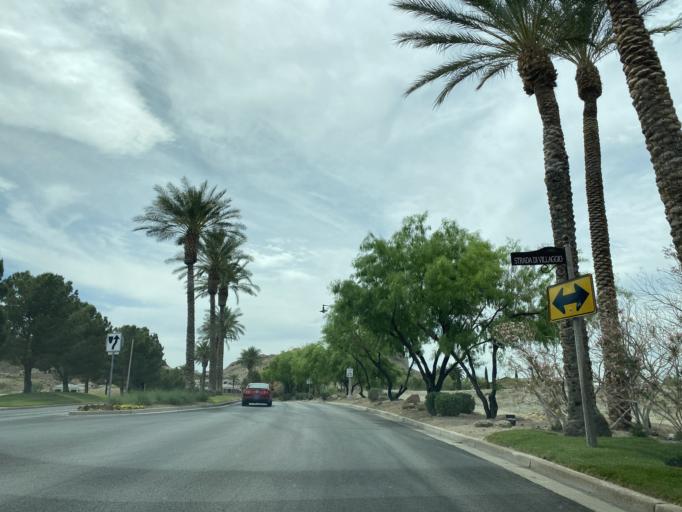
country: US
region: Nevada
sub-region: Clark County
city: Henderson
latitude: 36.1003
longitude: -114.9335
